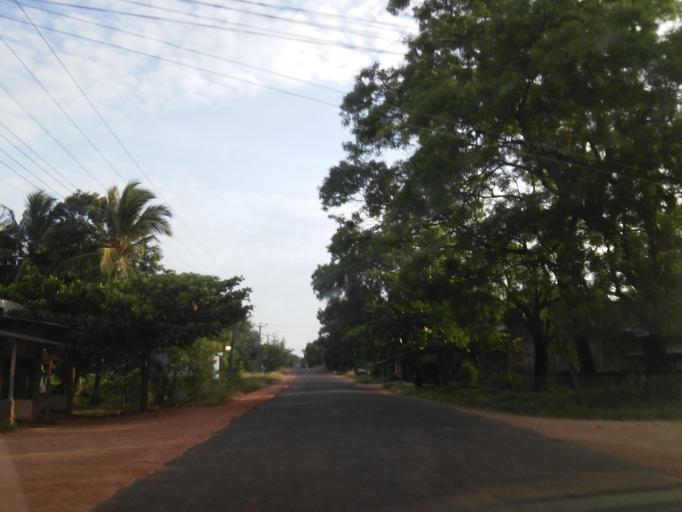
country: LK
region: Central
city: Sigiriya
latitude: 8.1244
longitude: 80.6329
